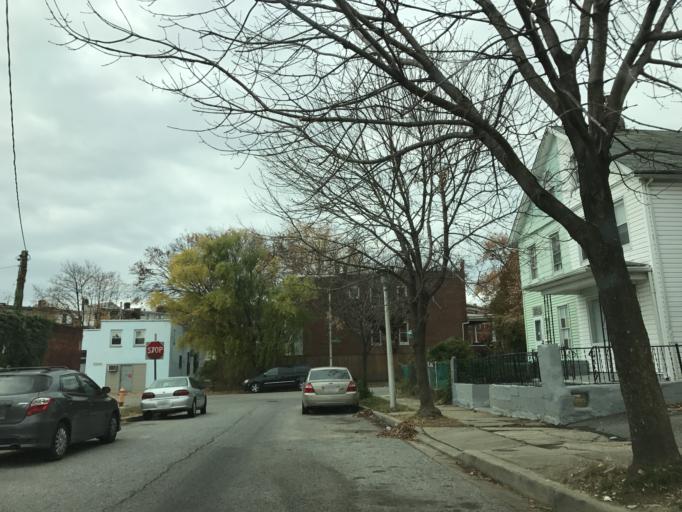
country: US
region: Maryland
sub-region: City of Baltimore
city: Baltimore
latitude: 39.3292
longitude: -76.6106
